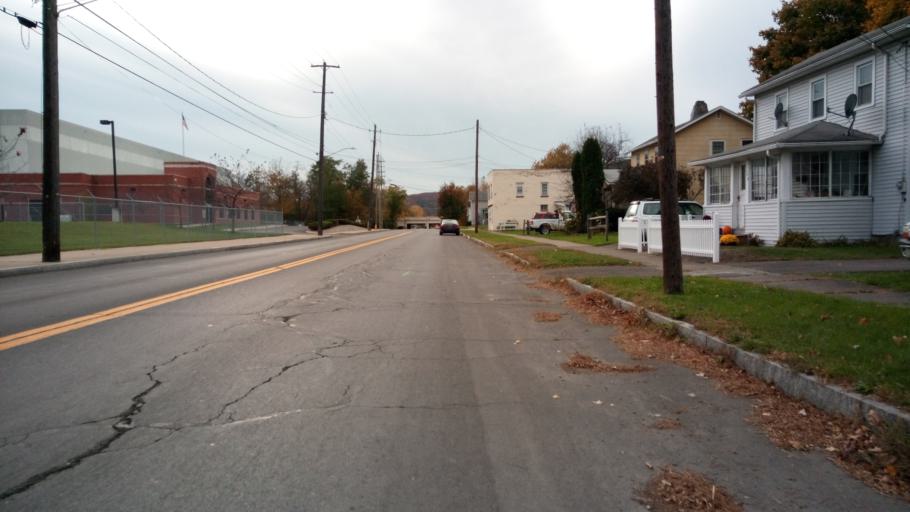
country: US
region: New York
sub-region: Chemung County
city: Elmira
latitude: 42.0760
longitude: -76.7953
